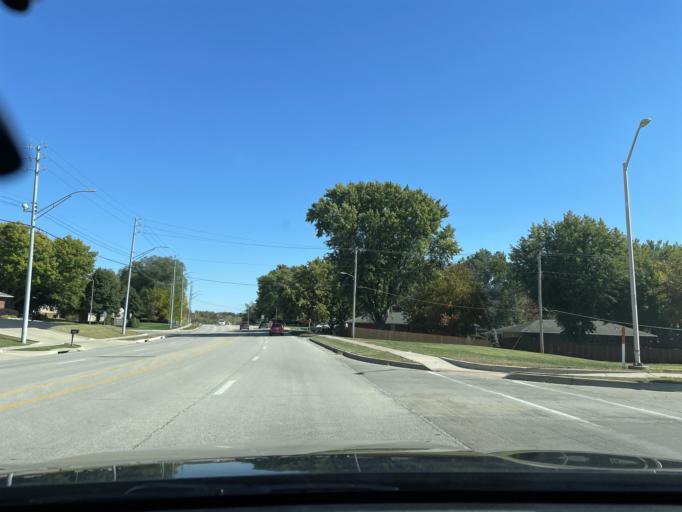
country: US
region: Missouri
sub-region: Andrew County
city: Country Club Village
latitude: 39.7809
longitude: -94.7736
